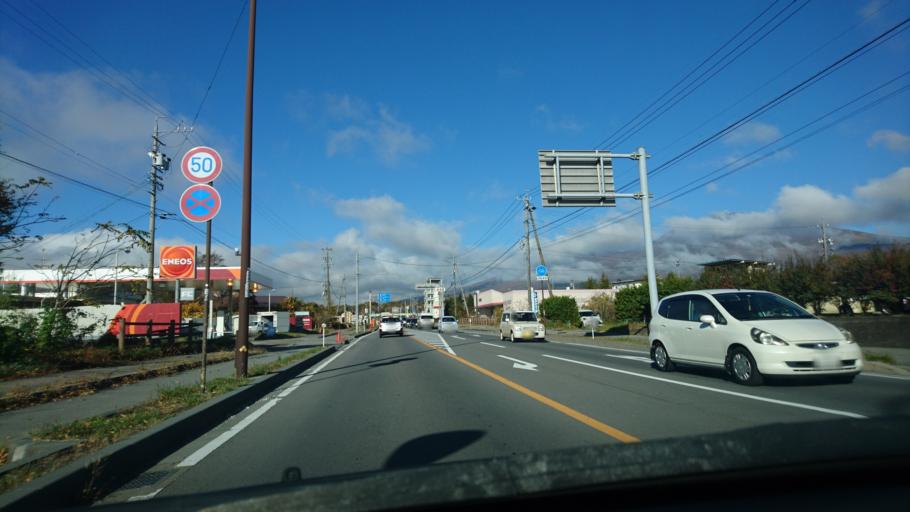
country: JP
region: Nagano
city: Komoro
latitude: 36.3373
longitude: 138.5917
